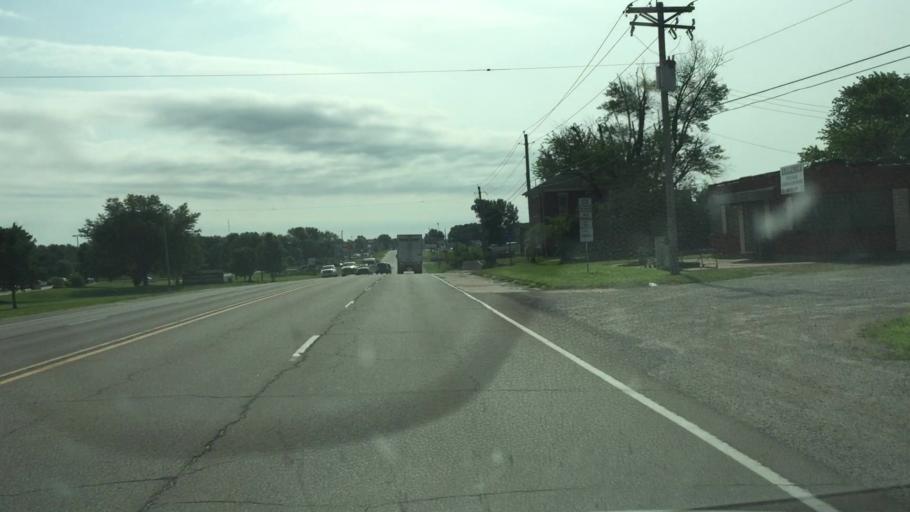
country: US
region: Iowa
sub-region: Lee County
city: Fort Madison
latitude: 40.6242
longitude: -91.3861
